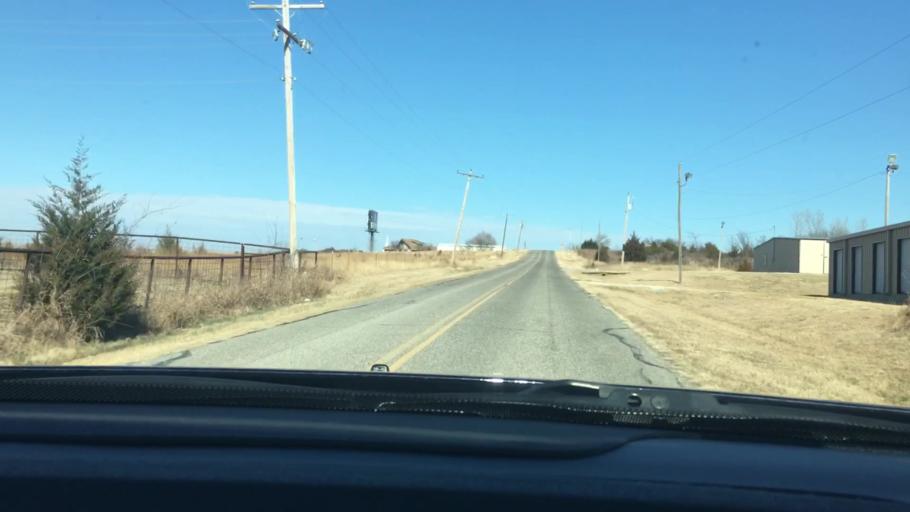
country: US
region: Oklahoma
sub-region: Murray County
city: Davis
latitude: 34.5023
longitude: -97.0553
